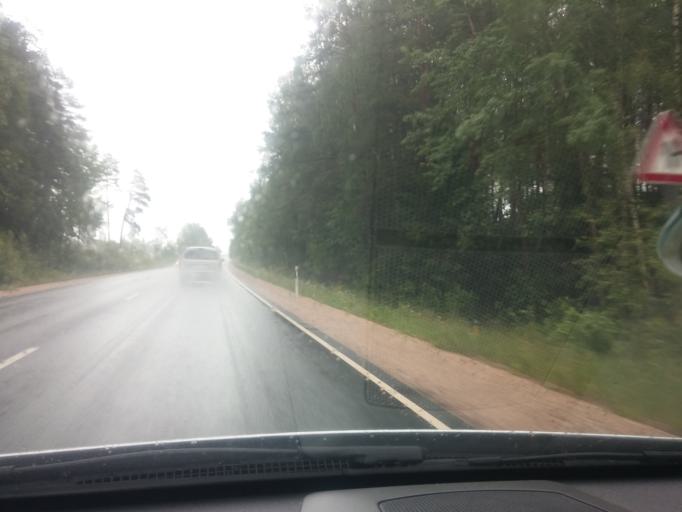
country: LV
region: Ikskile
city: Ikskile
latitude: 56.8749
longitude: 24.5306
